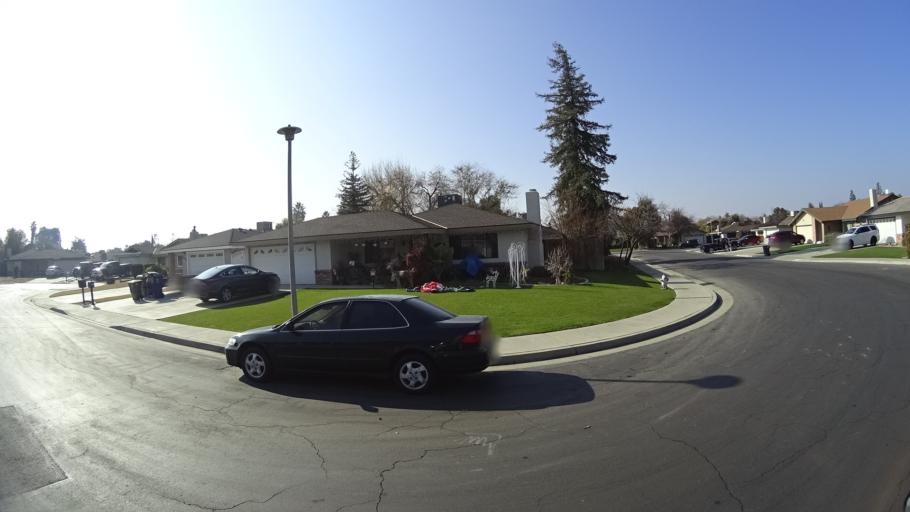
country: US
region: California
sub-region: Kern County
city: Greenacres
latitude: 35.3223
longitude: -119.0896
